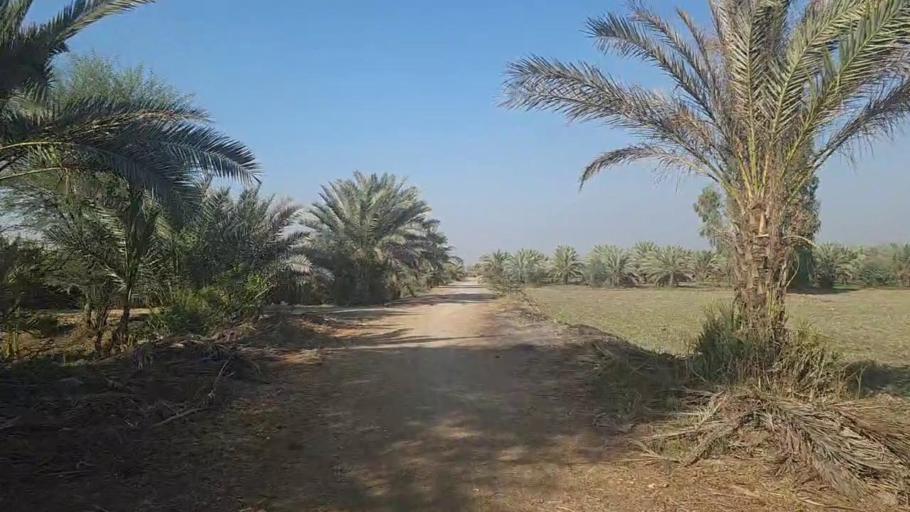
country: PK
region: Sindh
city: Kot Diji
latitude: 27.4311
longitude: 68.7377
